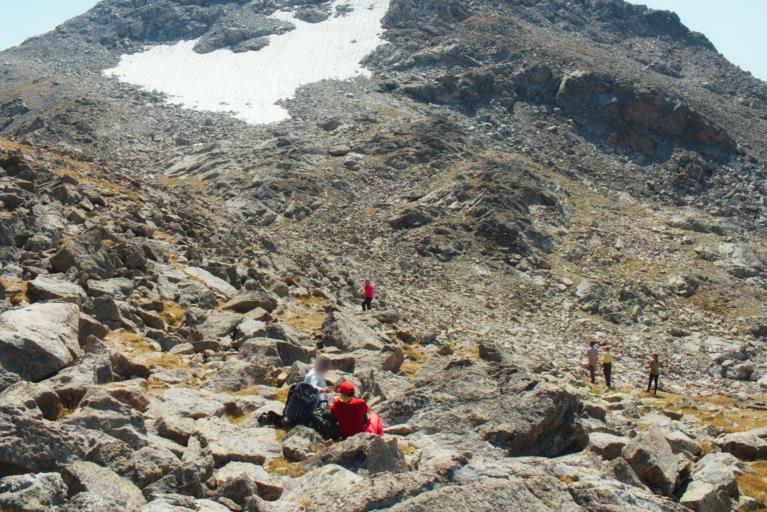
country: RU
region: Karachayevo-Cherkesiya
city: Nizhniy Arkhyz
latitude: 43.4575
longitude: 41.2167
